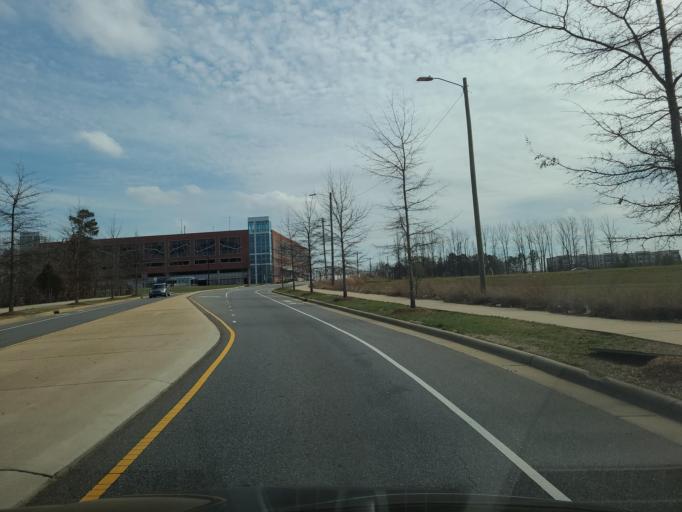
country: US
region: North Carolina
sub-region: Mecklenburg County
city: Charlotte
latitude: 35.2879
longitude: -80.7641
